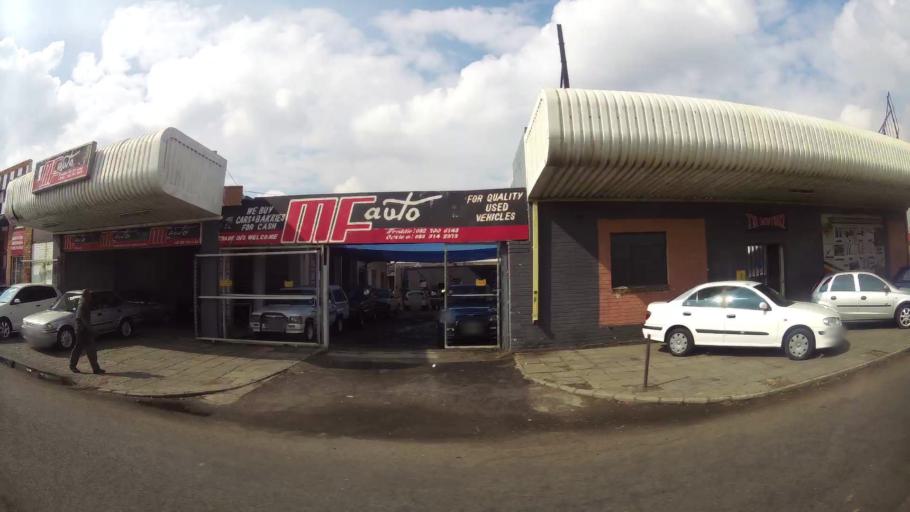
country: ZA
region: Gauteng
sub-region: Sedibeng District Municipality
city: Vereeniging
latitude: -26.6819
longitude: 27.9323
